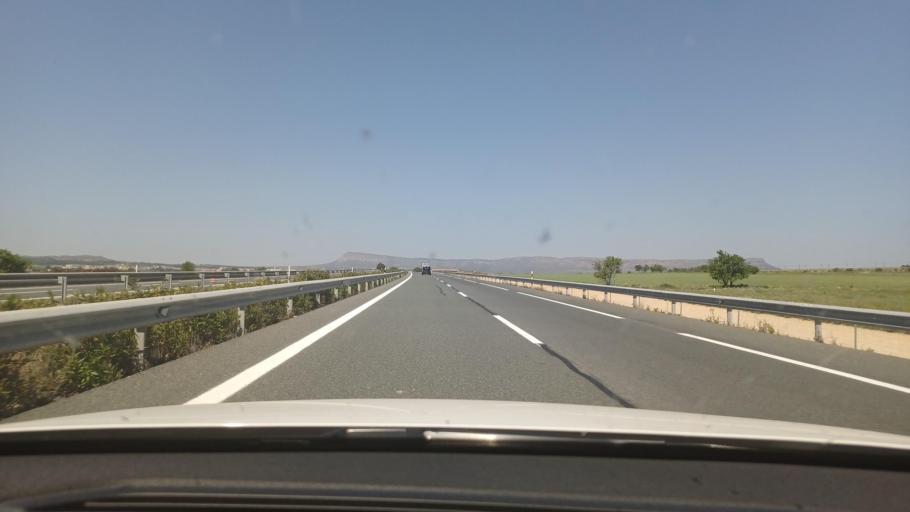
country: ES
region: Castille-La Mancha
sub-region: Provincia de Albacete
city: Almansa
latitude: 38.8606
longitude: -1.0391
